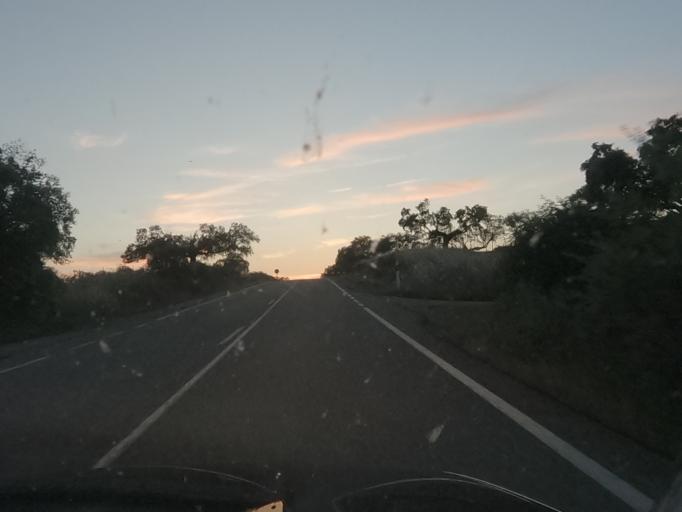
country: ES
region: Extremadura
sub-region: Provincia de Caceres
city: Piedras Albas
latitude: 39.7829
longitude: -6.9354
